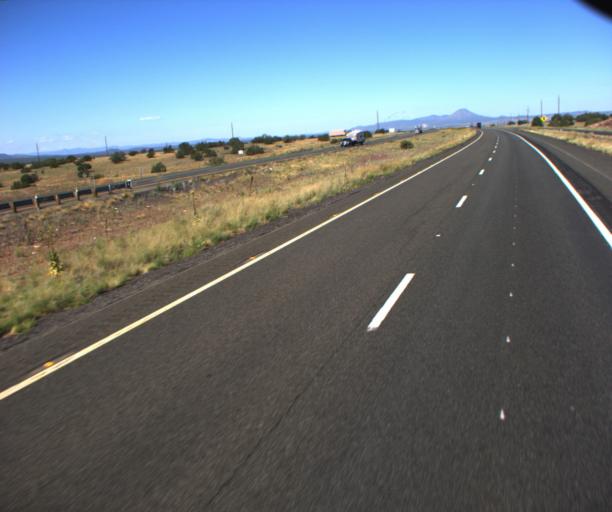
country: US
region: Arizona
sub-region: Coconino County
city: Williams
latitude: 35.2206
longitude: -112.4981
